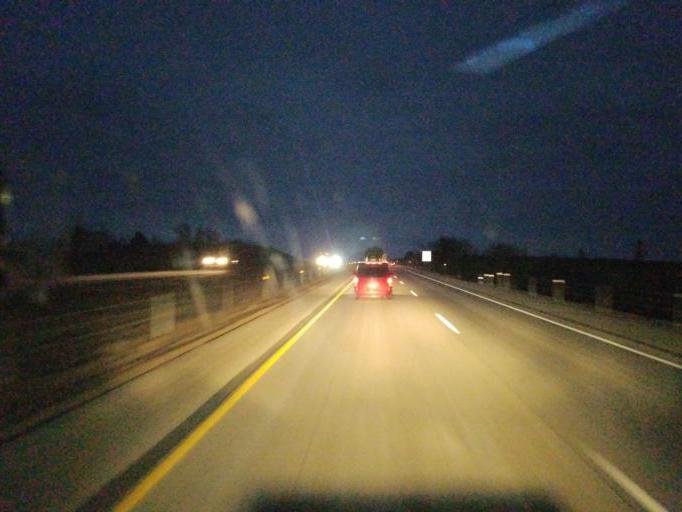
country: US
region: Iowa
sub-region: Guthrie County
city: Guthrie Center
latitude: 41.4930
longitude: -94.6035
